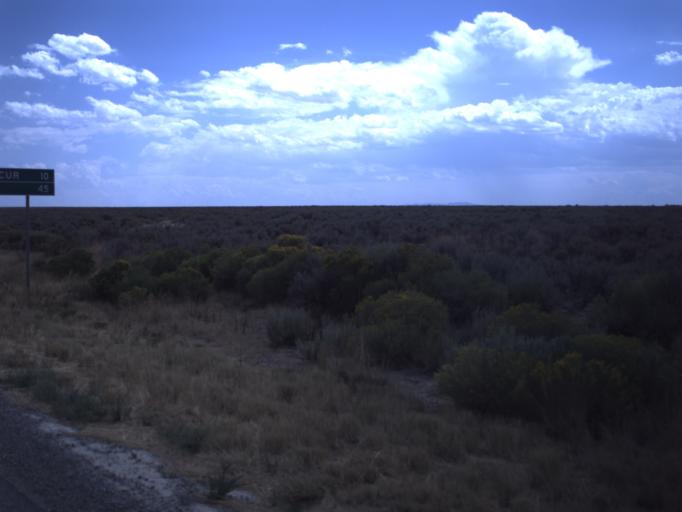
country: US
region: Utah
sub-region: Tooele County
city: Tooele
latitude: 40.3800
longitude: -112.3840
